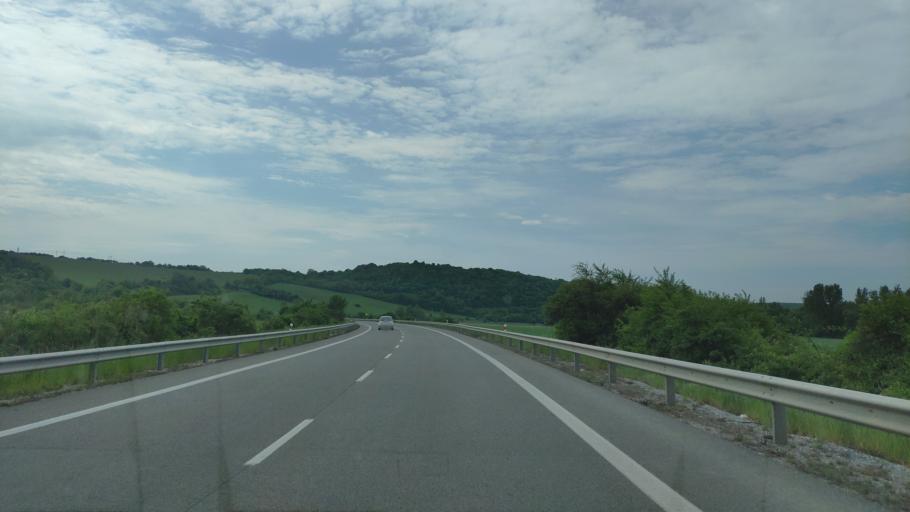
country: SK
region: Kosicky
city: Roznava
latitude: 48.5398
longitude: 20.3956
